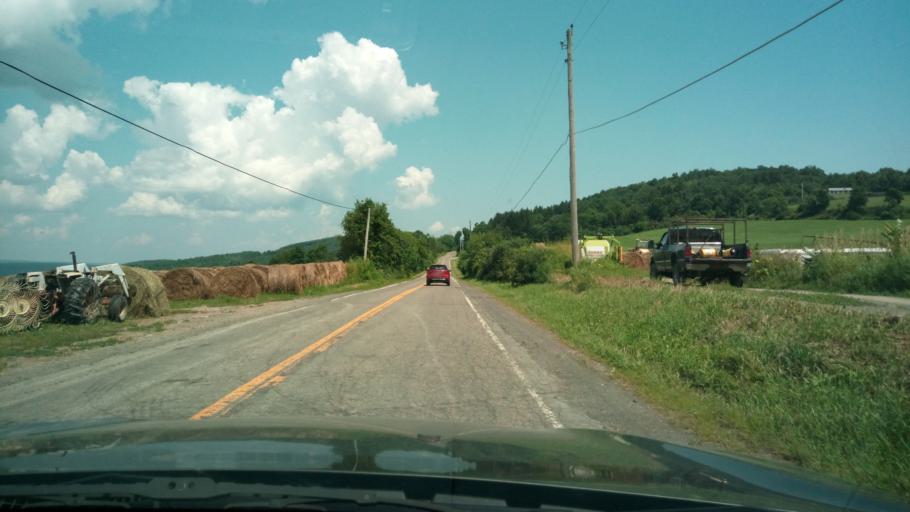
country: US
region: New York
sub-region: Chemung County
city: Horseheads North
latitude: 42.2565
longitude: -76.8013
